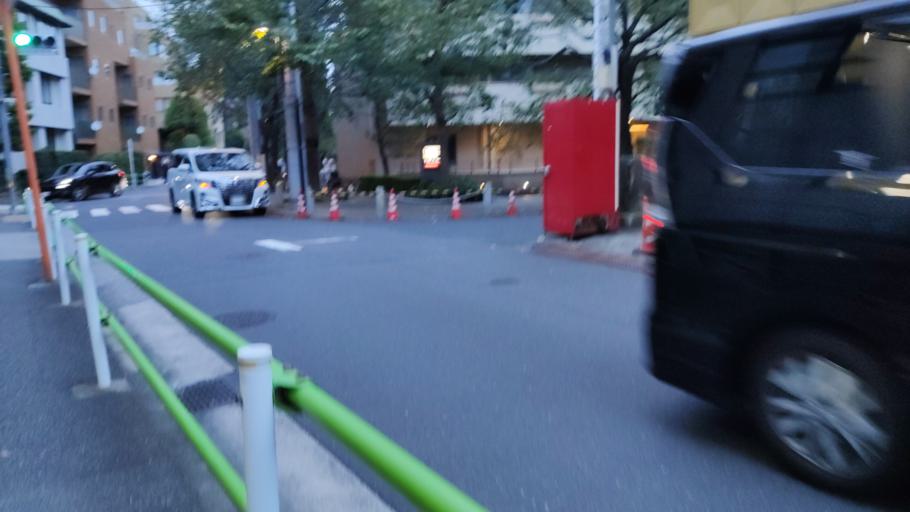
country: JP
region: Tokyo
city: Tokyo
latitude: 35.6535
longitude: 139.7310
